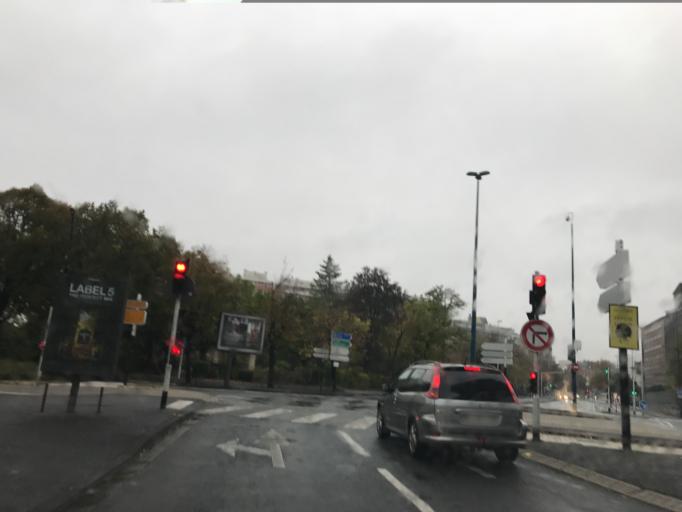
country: FR
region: Auvergne
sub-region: Departement du Puy-de-Dome
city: Clermont-Ferrand
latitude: 45.7776
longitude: 3.0962
